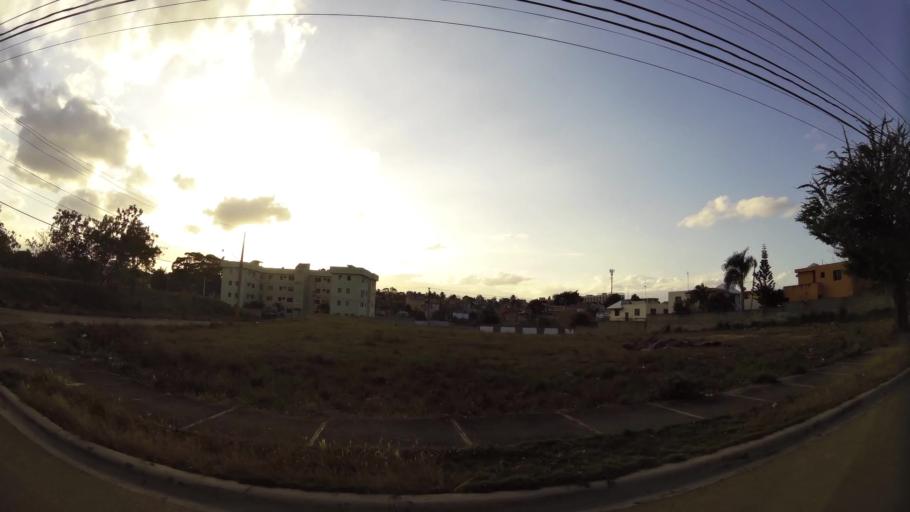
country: DO
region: Nacional
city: La Agustina
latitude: 18.5434
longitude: -69.9219
